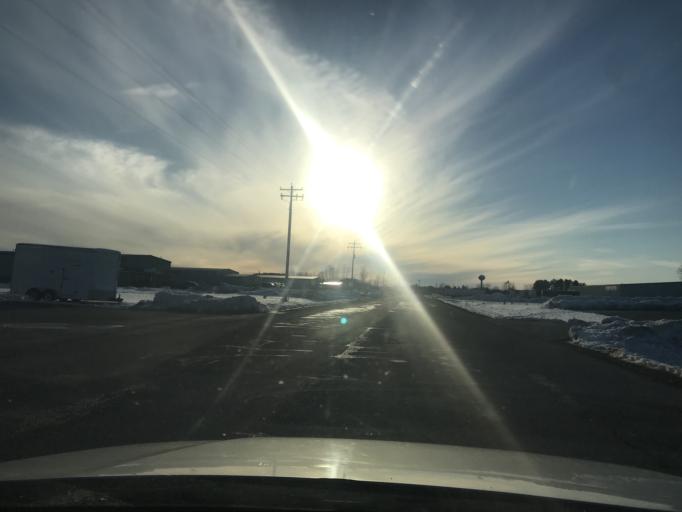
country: US
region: Wisconsin
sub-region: Marinette County
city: Peshtigo
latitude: 45.0570
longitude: -87.7237
